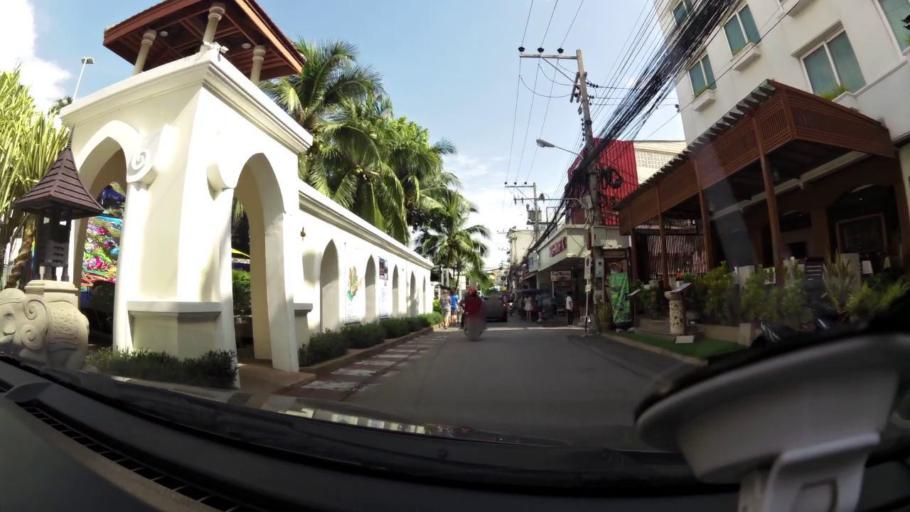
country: TH
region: Prachuap Khiri Khan
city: Hua Hin
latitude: 12.5704
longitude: 99.9600
